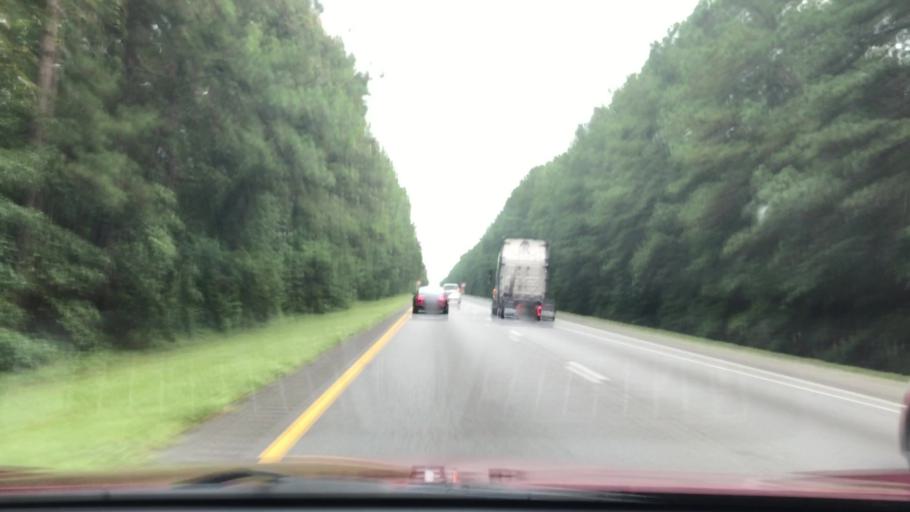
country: US
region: South Carolina
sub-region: Dorchester County
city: Ridgeville
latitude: 33.1057
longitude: -80.2509
